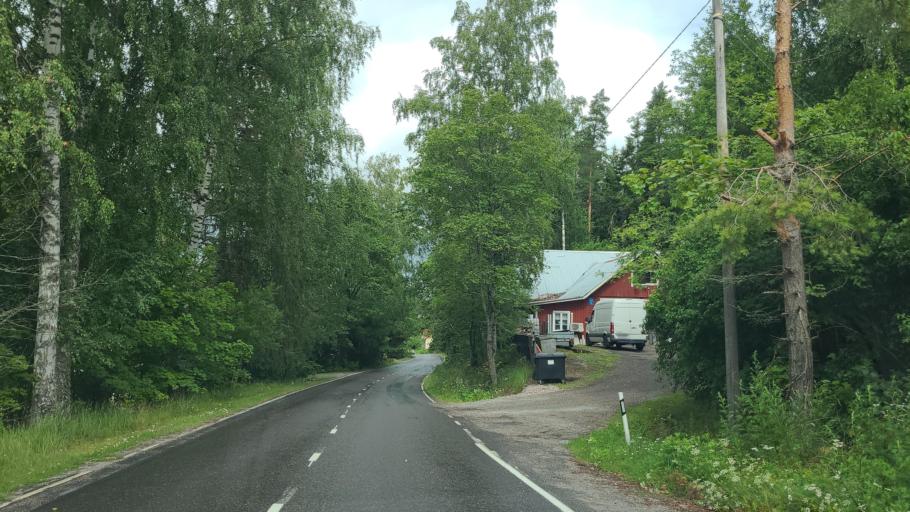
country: FI
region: Varsinais-Suomi
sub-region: Turku
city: Sauvo
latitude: 60.3382
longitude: 22.7044
